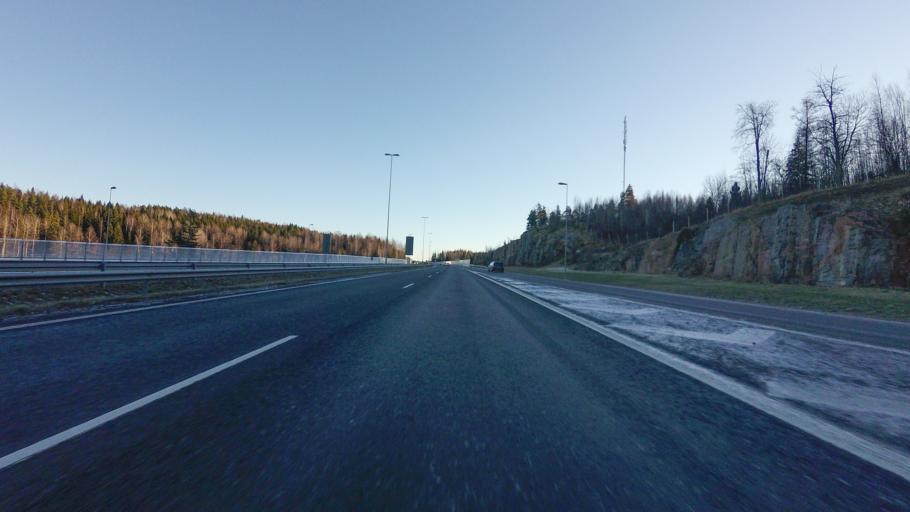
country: FI
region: Uusimaa
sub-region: Helsinki
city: Lohja
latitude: 60.2920
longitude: 24.0699
